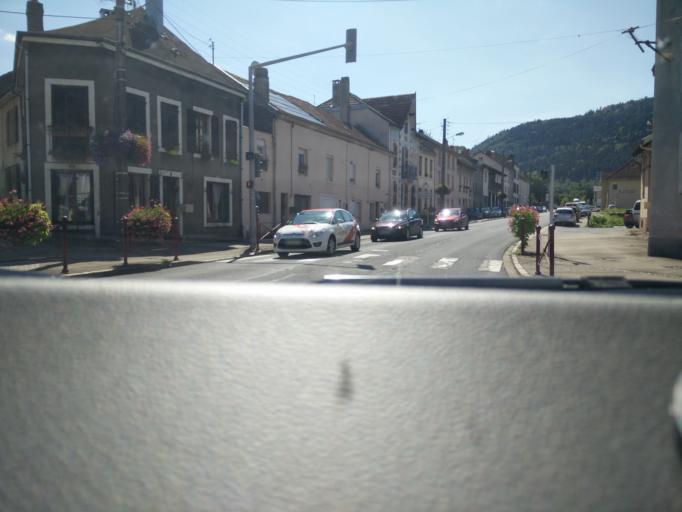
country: FR
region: Lorraine
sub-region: Departement des Vosges
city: Etival-Clairefontaine
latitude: 48.4046
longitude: 6.8473
